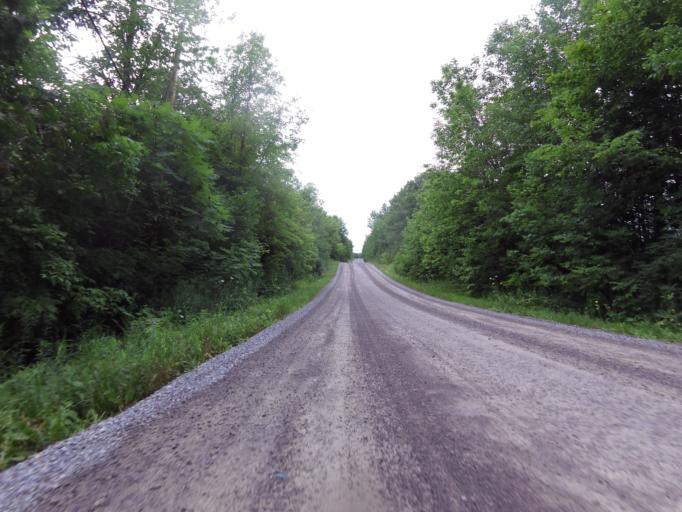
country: CA
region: Ontario
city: Carleton Place
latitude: 45.1508
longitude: -76.2334
